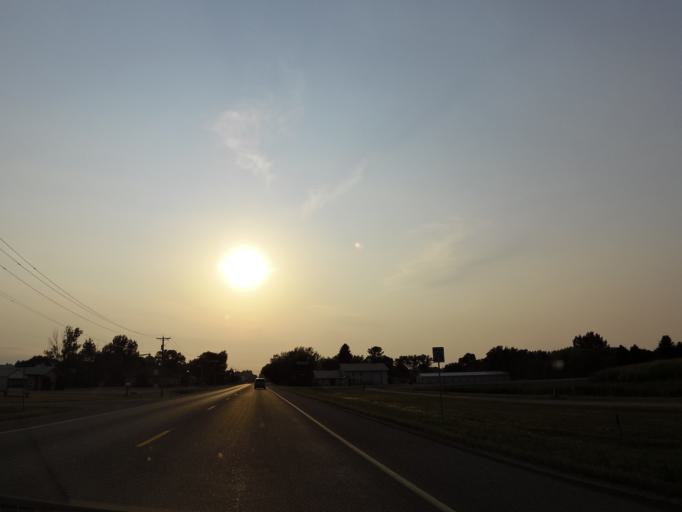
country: US
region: North Dakota
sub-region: Traill County
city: Mayville
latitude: 47.4985
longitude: -97.3621
